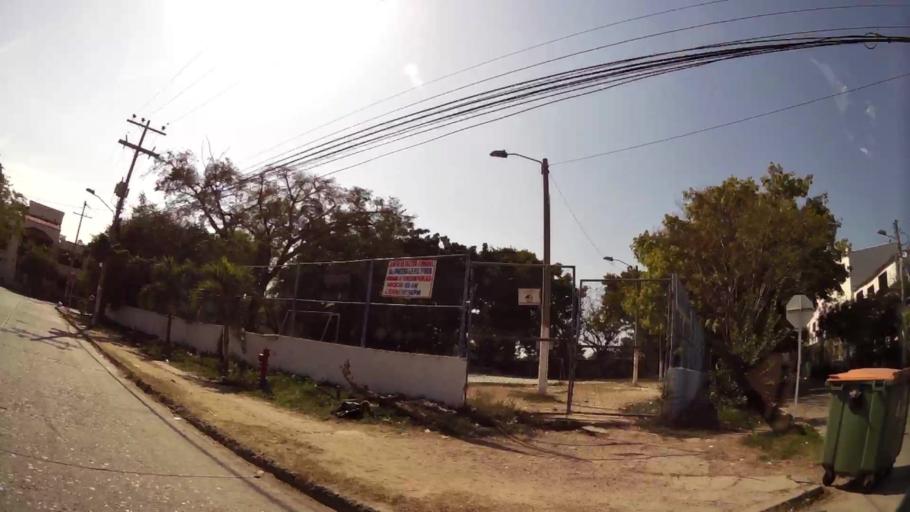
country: CO
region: Bolivar
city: Cartagena
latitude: 10.3861
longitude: -75.4730
